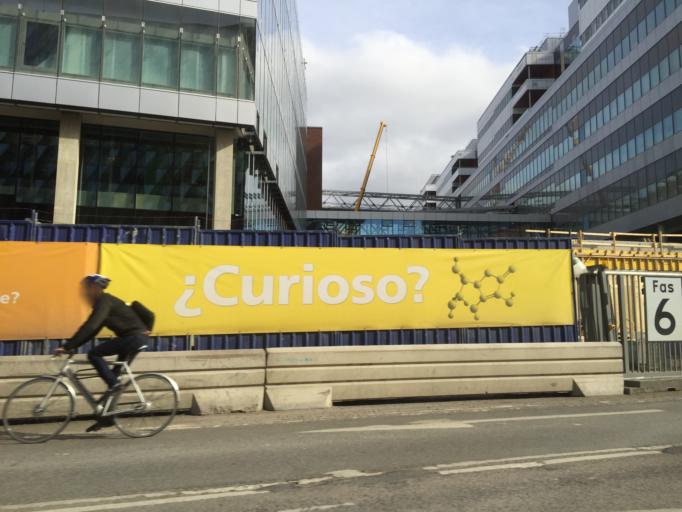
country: SE
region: Stockholm
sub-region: Solna Kommun
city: Solna
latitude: 59.3489
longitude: 18.0281
